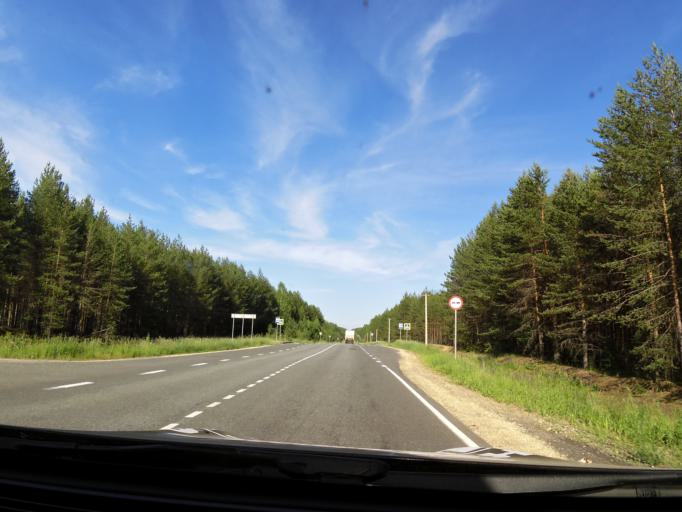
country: RU
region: Kirov
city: Belaya Kholunitsa
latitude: 58.9117
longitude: 51.0681
